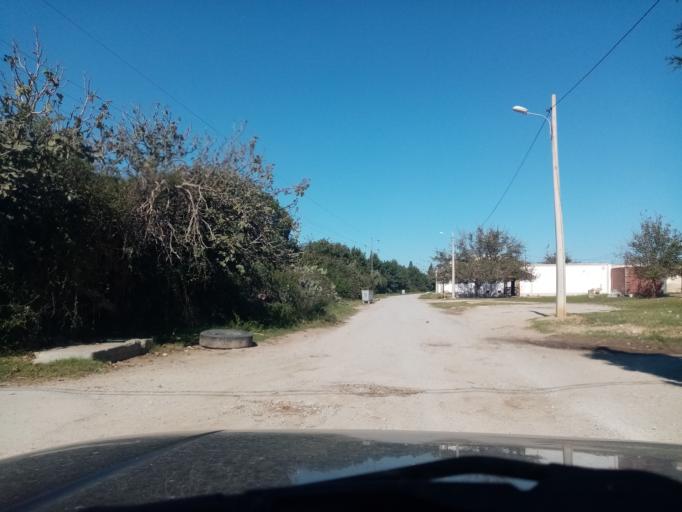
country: TN
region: Nabul
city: Bu `Urqub
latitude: 36.5721
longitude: 10.5748
